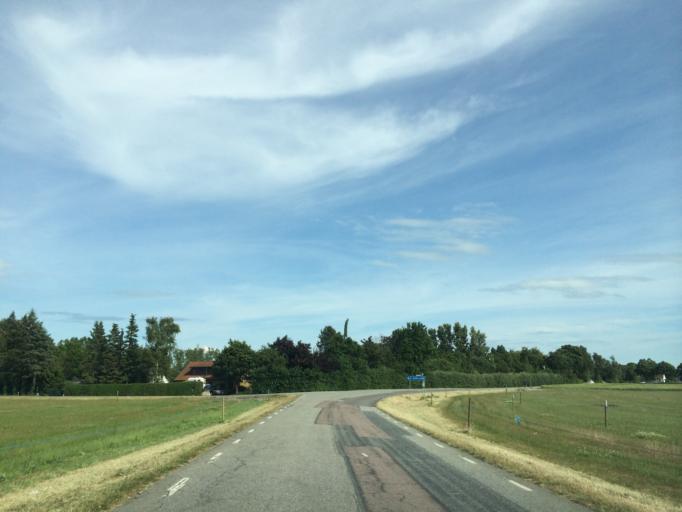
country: SE
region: Skane
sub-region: Kavlinge Kommun
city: Loddekopinge
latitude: 55.7425
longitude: 13.0584
